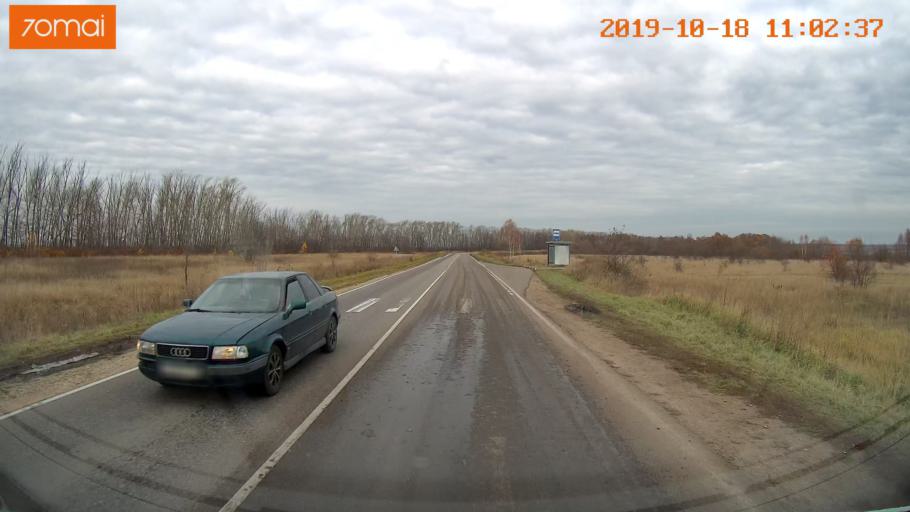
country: RU
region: Tula
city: Yepifan'
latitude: 53.8683
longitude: 38.5439
